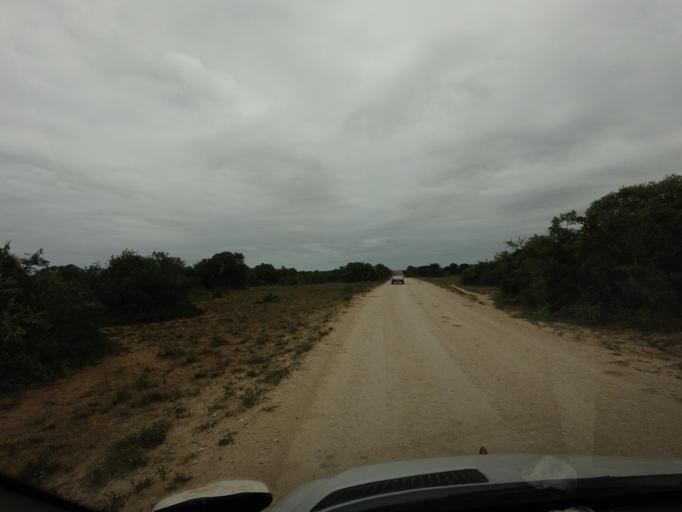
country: ZA
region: Eastern Cape
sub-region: Cacadu District Municipality
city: Kirkwood
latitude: -33.4856
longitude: 25.7716
